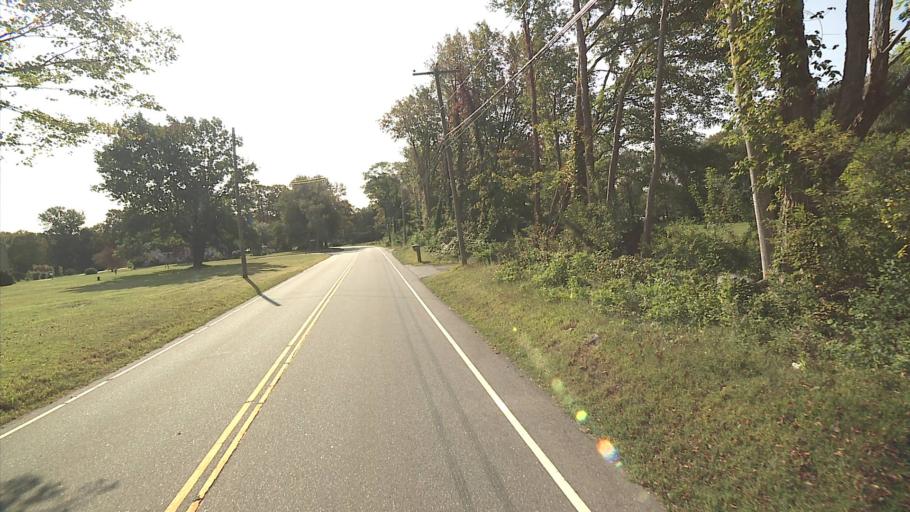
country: US
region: Connecticut
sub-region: Windham County
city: Willimantic
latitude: 41.6790
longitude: -72.2754
